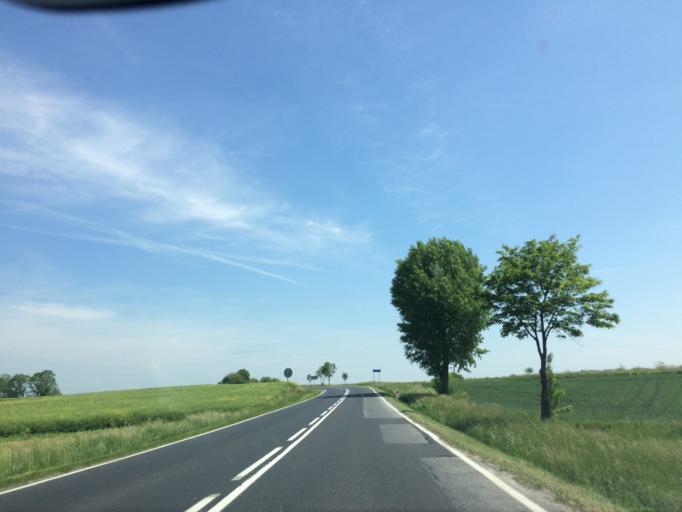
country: PL
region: Lower Silesian Voivodeship
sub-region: Powiat wroclawski
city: Gniechowice
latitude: 50.9709
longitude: 16.8063
